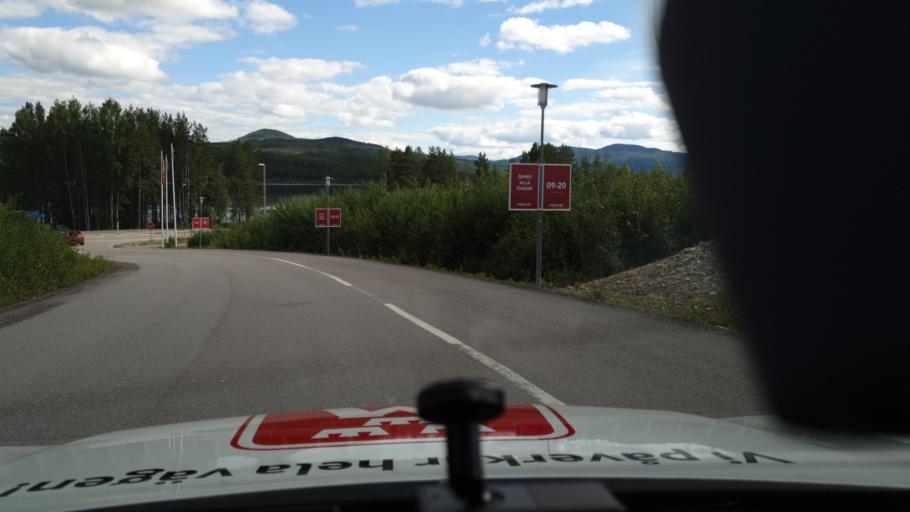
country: NO
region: Hedmark
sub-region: Trysil
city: Innbygda
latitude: 61.0462
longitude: 12.5940
